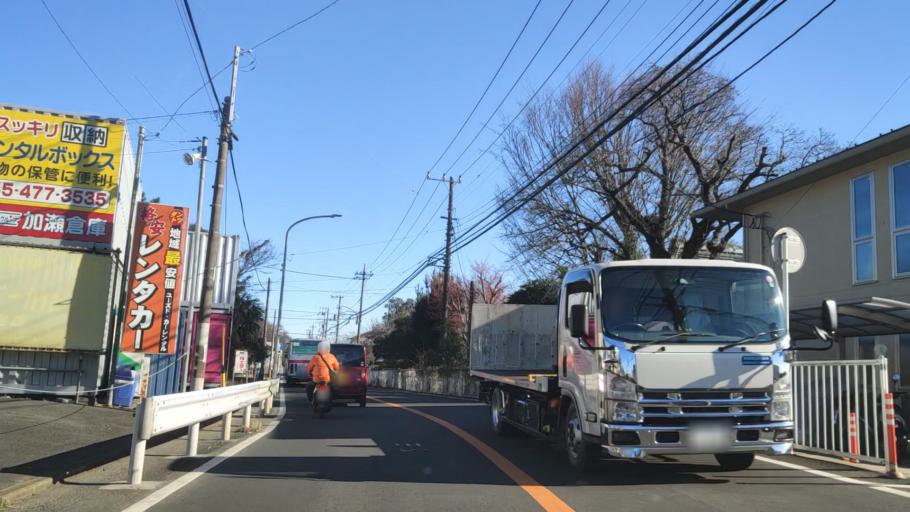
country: JP
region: Tokyo
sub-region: Machida-shi
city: Machida
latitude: 35.5283
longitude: 139.5239
